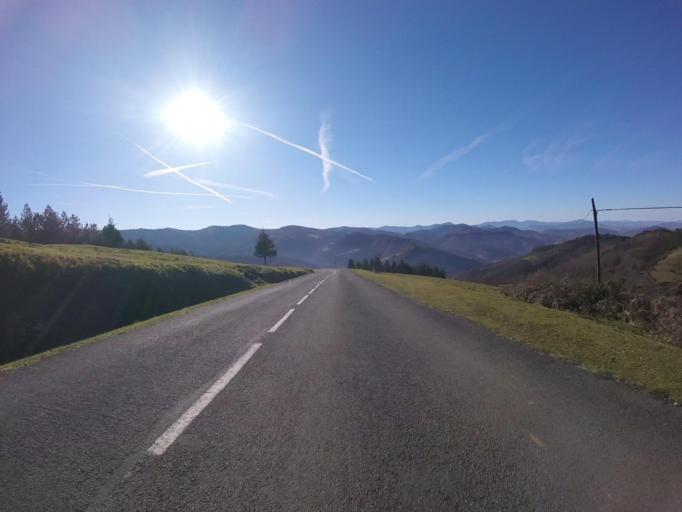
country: ES
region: Basque Country
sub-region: Provincia de Guipuzcoa
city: Irun
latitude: 43.2935
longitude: -1.8073
